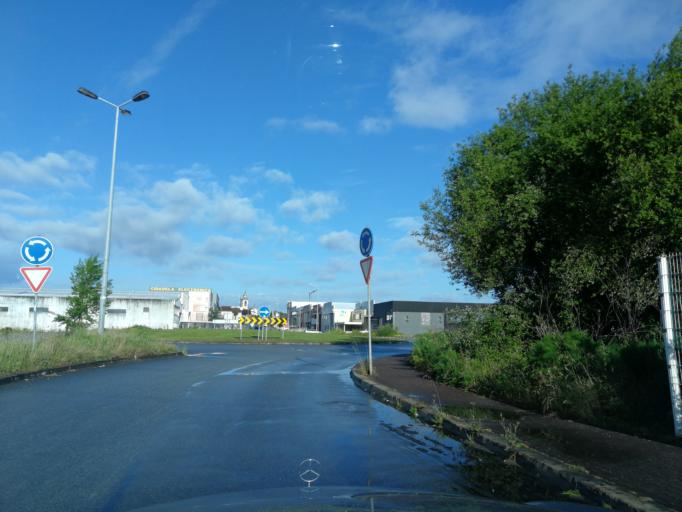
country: PT
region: Braga
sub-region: Braga
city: Braga
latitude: 41.5657
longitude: -8.4467
